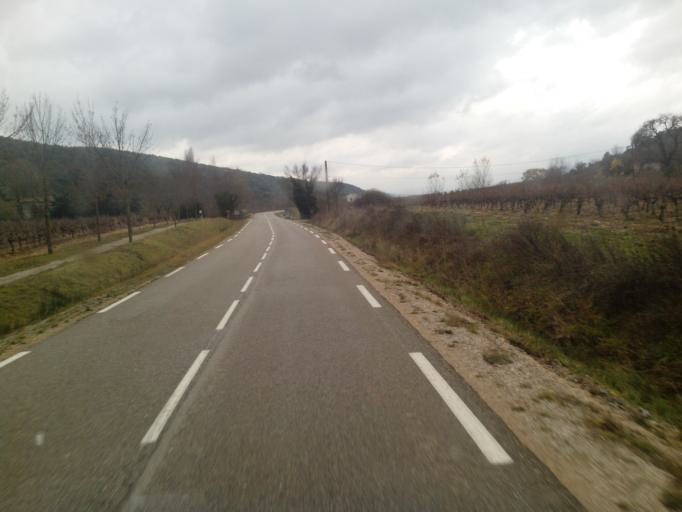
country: FR
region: Languedoc-Roussillon
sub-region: Departement de l'Herault
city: Saint-Bauzille-de-Putois
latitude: 43.9239
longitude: 3.7919
